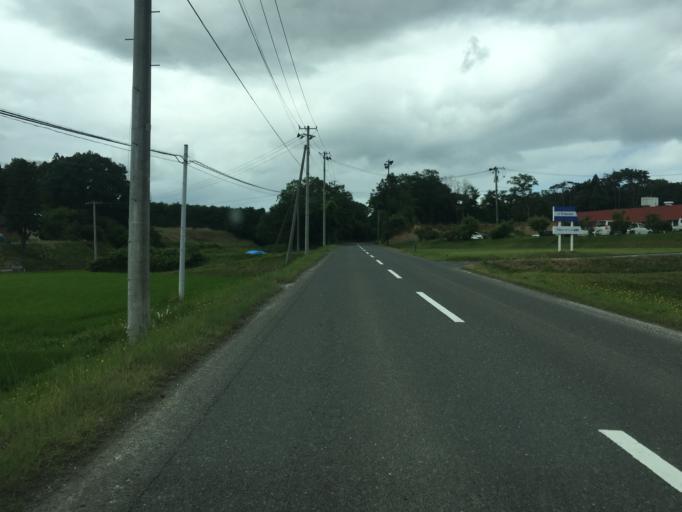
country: JP
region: Miyagi
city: Marumori
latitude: 37.7479
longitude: 140.9632
